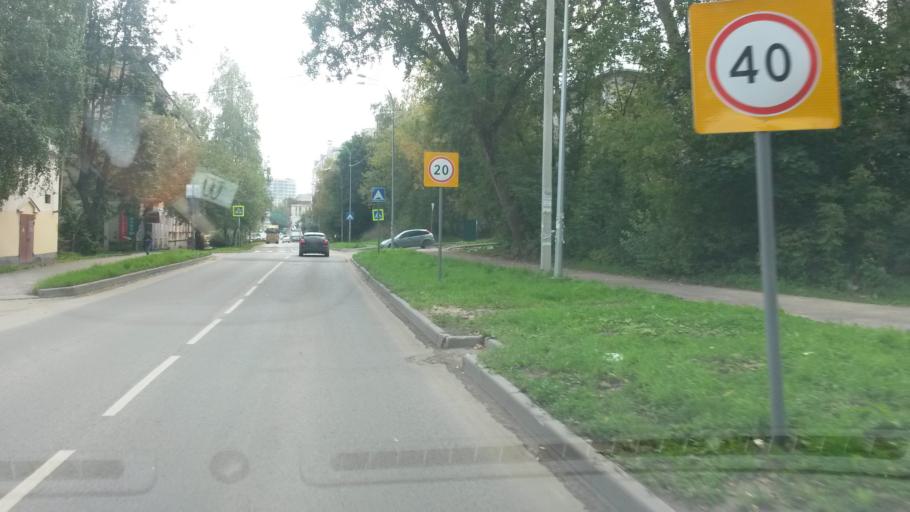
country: RU
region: Ivanovo
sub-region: Gorod Ivanovo
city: Ivanovo
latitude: 57.0046
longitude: 40.9632
